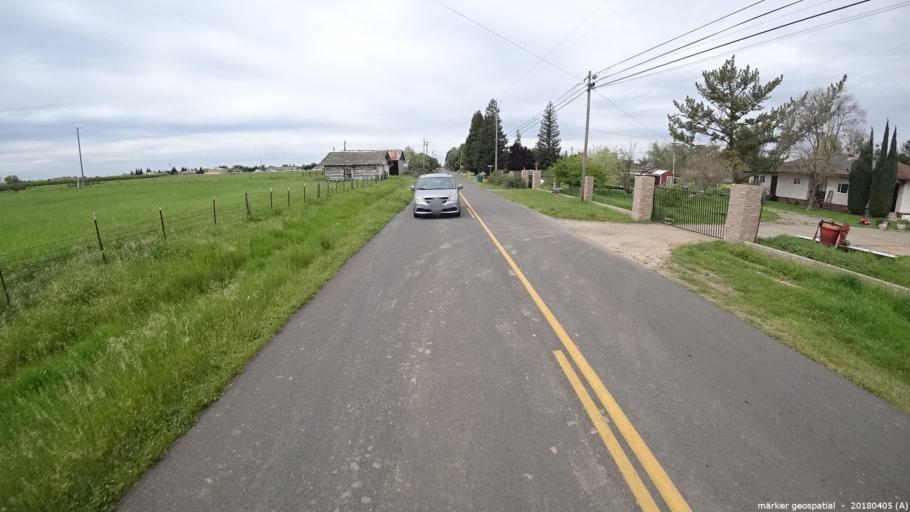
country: US
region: California
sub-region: Sacramento County
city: Galt
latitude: 38.2838
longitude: -121.3141
